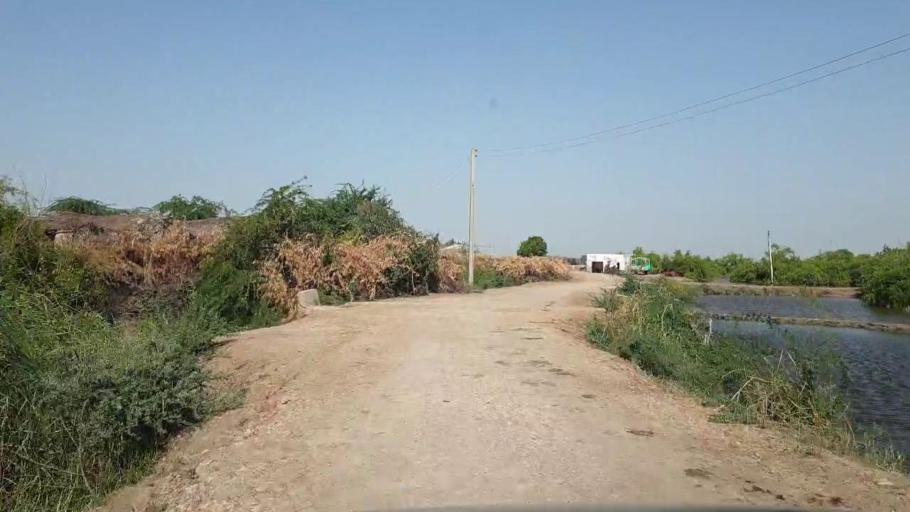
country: PK
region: Sindh
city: Tando Bago
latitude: 24.7545
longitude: 69.0277
